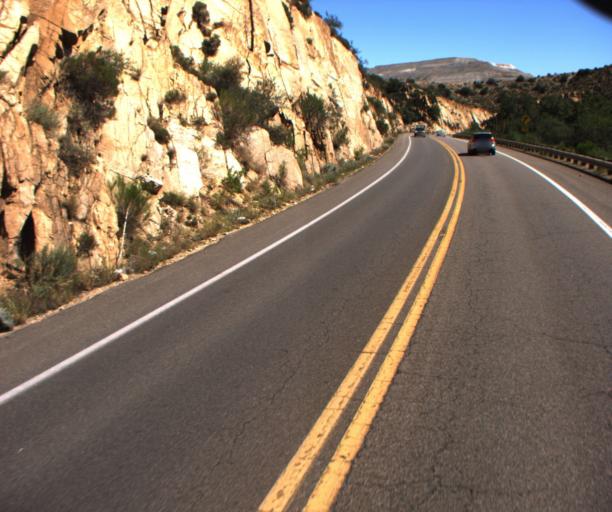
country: US
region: Arizona
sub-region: Gila County
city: Miami
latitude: 33.3788
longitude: -110.9077
